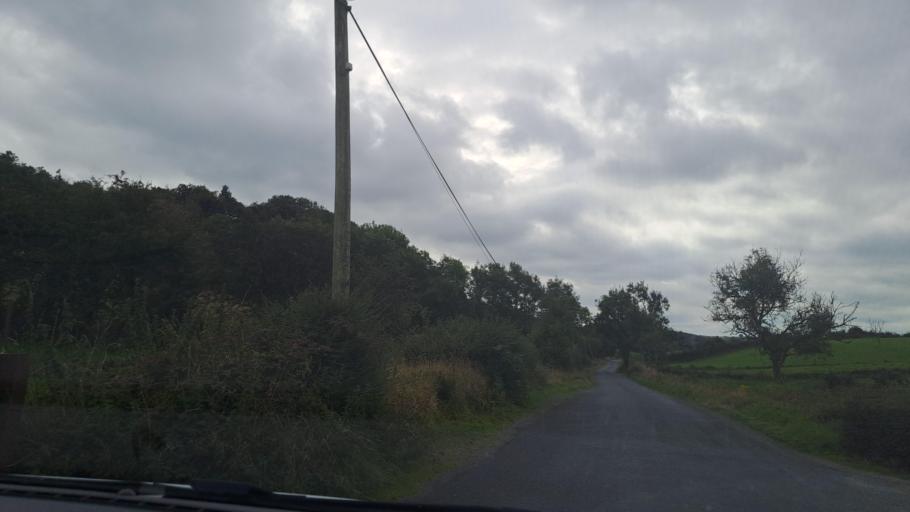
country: IE
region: Ulster
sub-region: An Cabhan
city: Bailieborough
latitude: 53.9450
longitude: -6.9075
